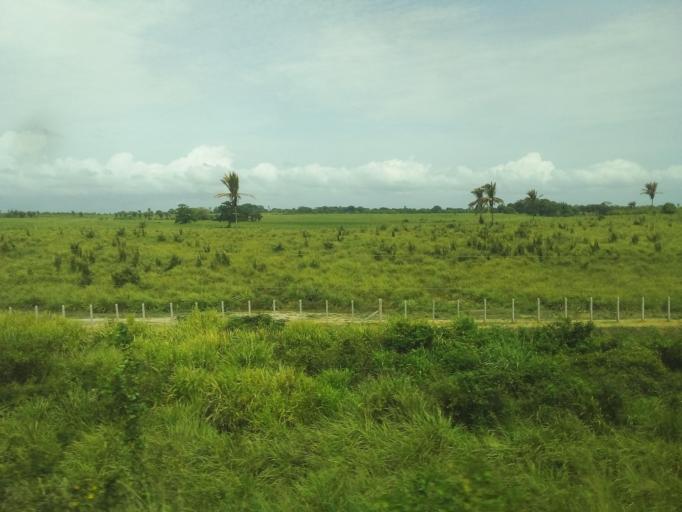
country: BR
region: Maranhao
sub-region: Anajatuba
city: Anajatuba
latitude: -3.4545
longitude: -44.5861
